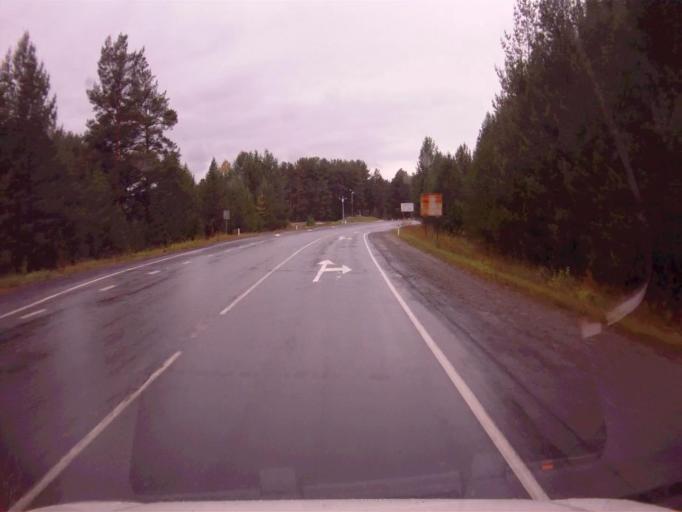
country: RU
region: Chelyabinsk
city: Verkhniy Ufaley
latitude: 56.0274
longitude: 60.2886
